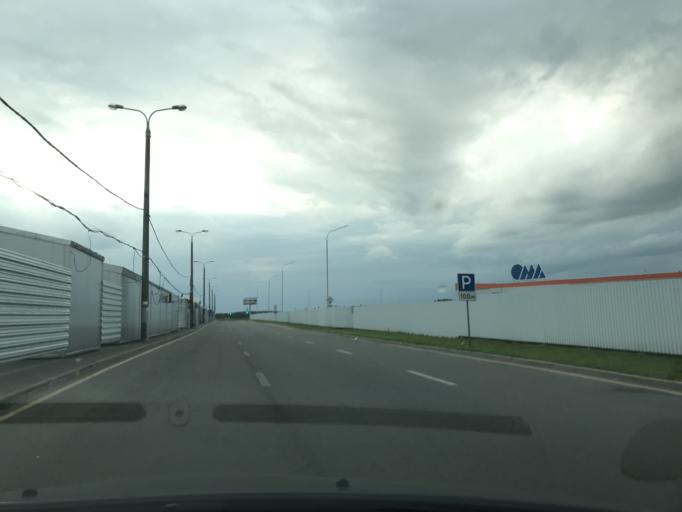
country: BY
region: Minsk
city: Borovlyany
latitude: 53.9652
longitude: 27.6261
